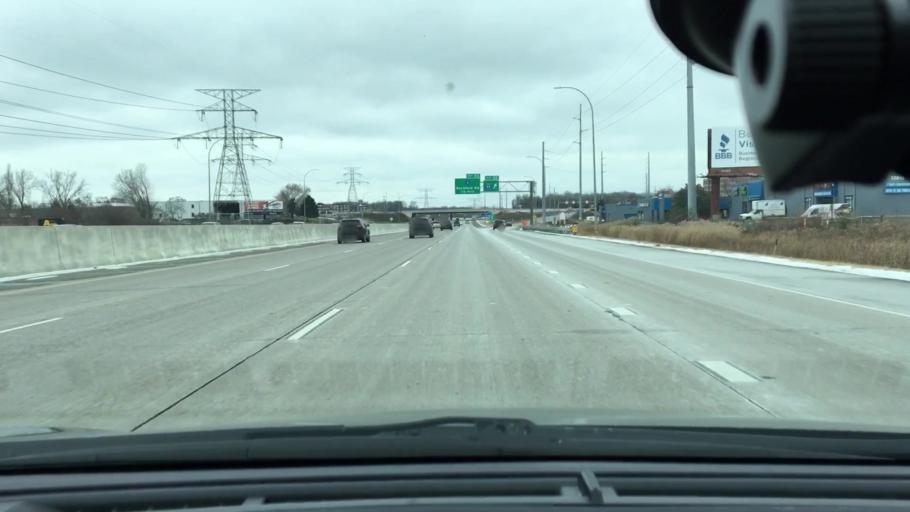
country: US
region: Minnesota
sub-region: Hennepin County
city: Plymouth
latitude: 45.0050
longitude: -93.4571
